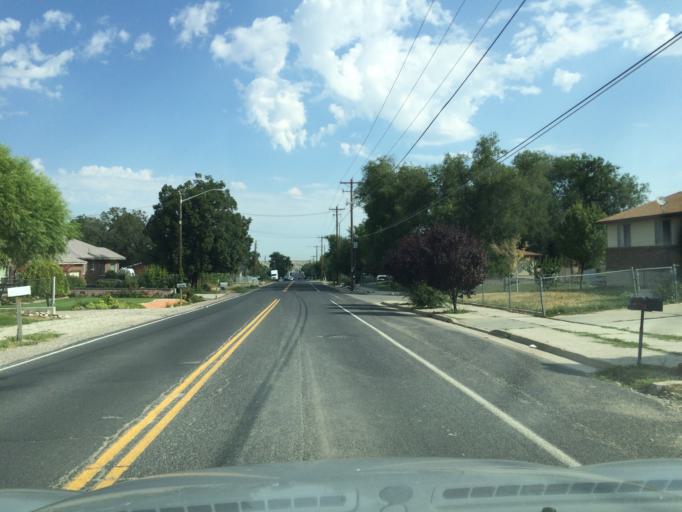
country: US
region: Utah
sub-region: Salt Lake County
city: West Valley City
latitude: 40.6982
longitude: -112.0439
